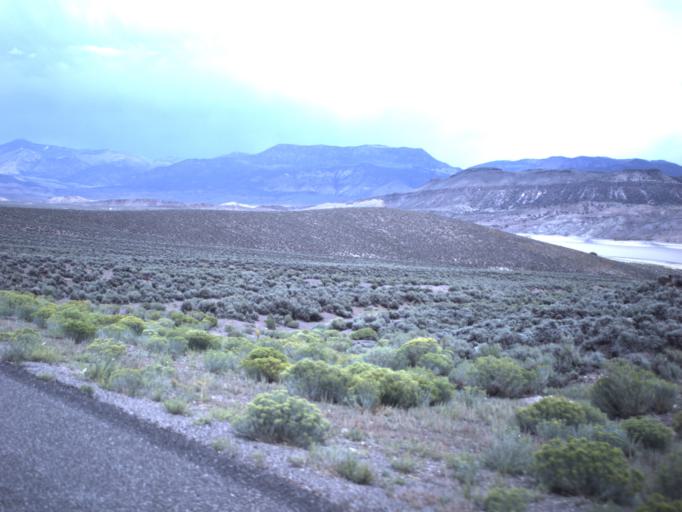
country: US
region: Utah
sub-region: Piute County
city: Junction
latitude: 38.3029
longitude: -112.2239
